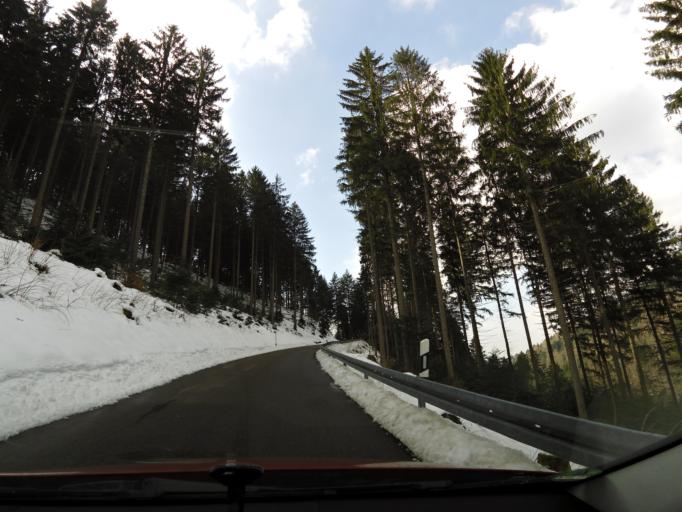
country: DE
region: Baden-Wuerttemberg
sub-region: Freiburg Region
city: Seebach
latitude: 48.5444
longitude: 8.1881
